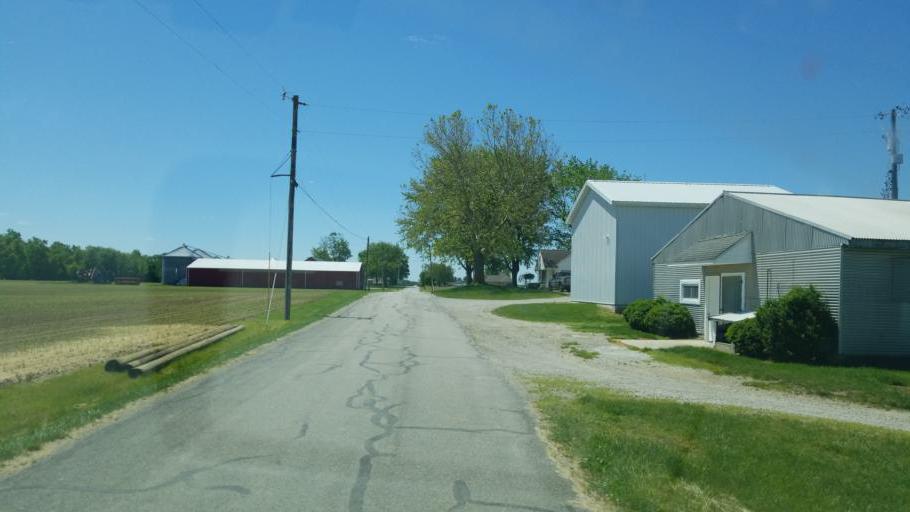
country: US
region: Ohio
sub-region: Shelby County
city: Fort Loramie
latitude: 40.3751
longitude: -84.3166
